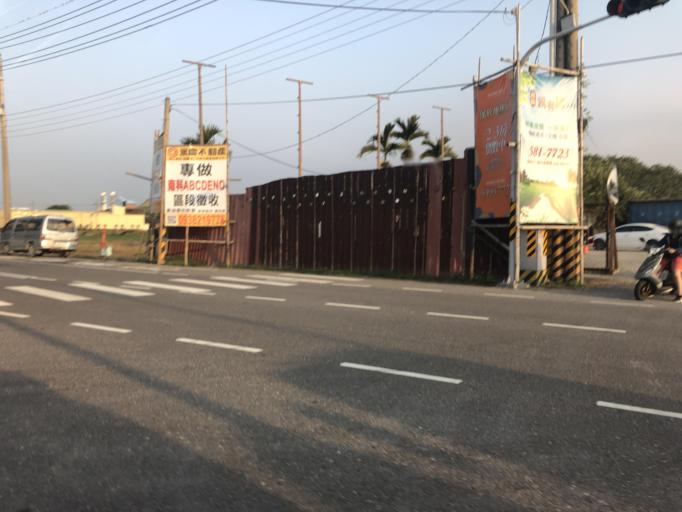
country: TW
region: Taiwan
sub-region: Tainan
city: Tainan
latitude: 23.1246
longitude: 120.2509
